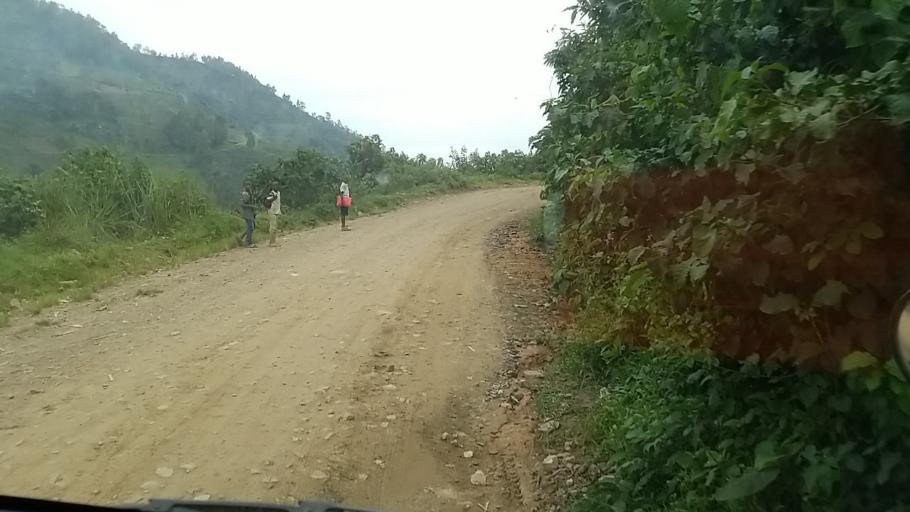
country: CD
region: Nord Kivu
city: Sake
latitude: -1.9543
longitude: 28.9257
